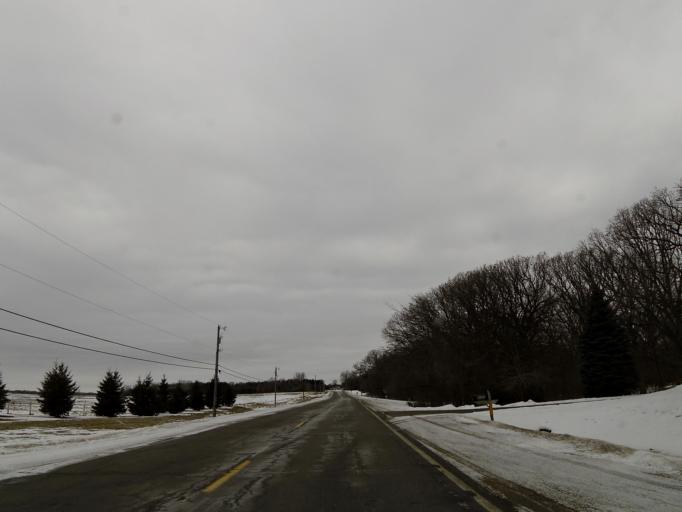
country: US
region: Minnesota
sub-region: Washington County
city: Cottage Grove
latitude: 44.8144
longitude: -92.8925
